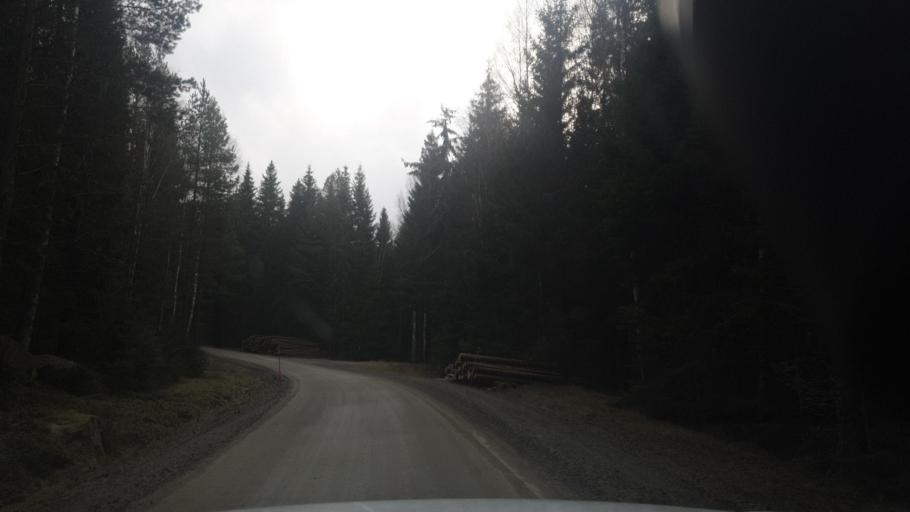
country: SE
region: Vaermland
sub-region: Eda Kommun
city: Amotfors
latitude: 59.8543
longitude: 12.5089
